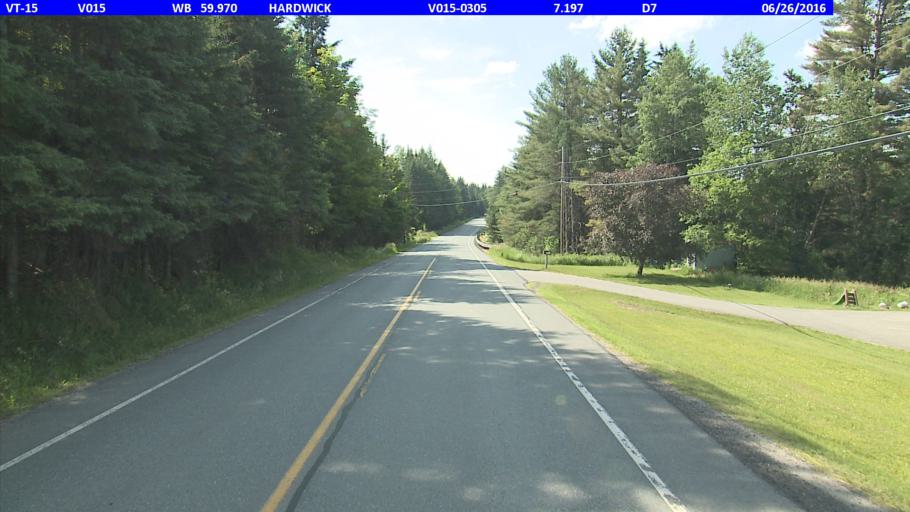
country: US
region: Vermont
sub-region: Caledonia County
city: Hardwick
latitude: 44.4843
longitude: -72.3056
